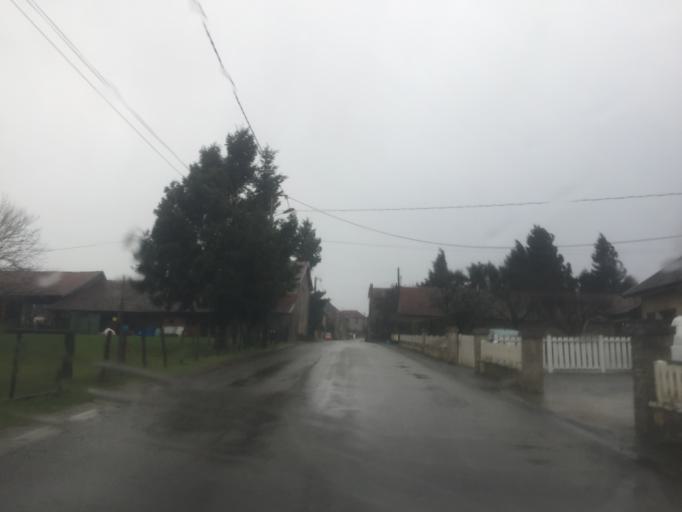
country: FR
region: Franche-Comte
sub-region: Departement du Jura
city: Dampierre
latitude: 47.2190
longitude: 5.7348
